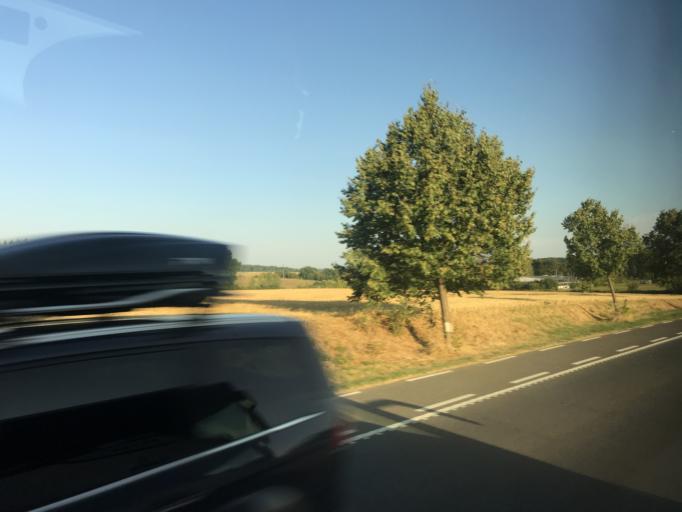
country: LU
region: Luxembourg
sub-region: Canton de Luxembourg
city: Weiler-la-Tour
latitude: 49.5371
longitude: 6.1777
